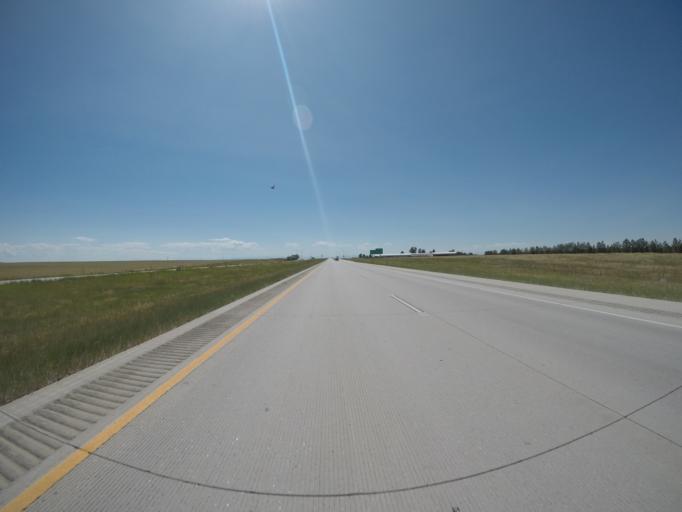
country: US
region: Colorado
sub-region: Adams County
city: Bennett
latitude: 39.7387
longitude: -104.5188
